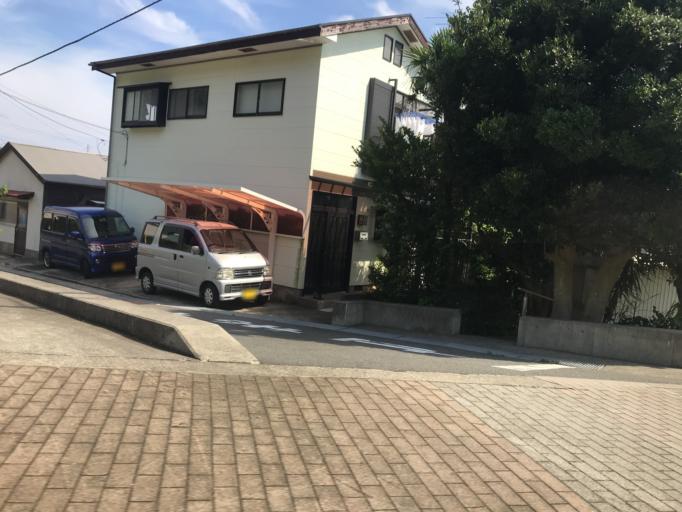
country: JP
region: Shizuoka
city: Ito
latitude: 34.7825
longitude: 139.4143
